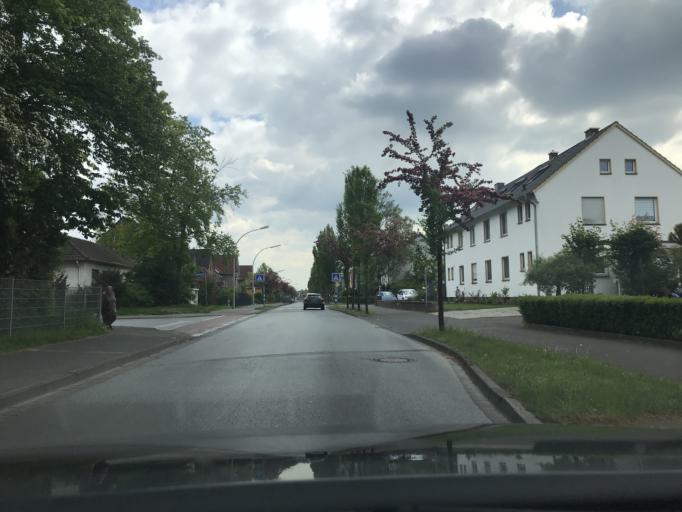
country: DE
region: North Rhine-Westphalia
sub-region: Regierungsbezirk Detmold
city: Rheda-Wiedenbruck
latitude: 51.8525
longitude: 8.2776
